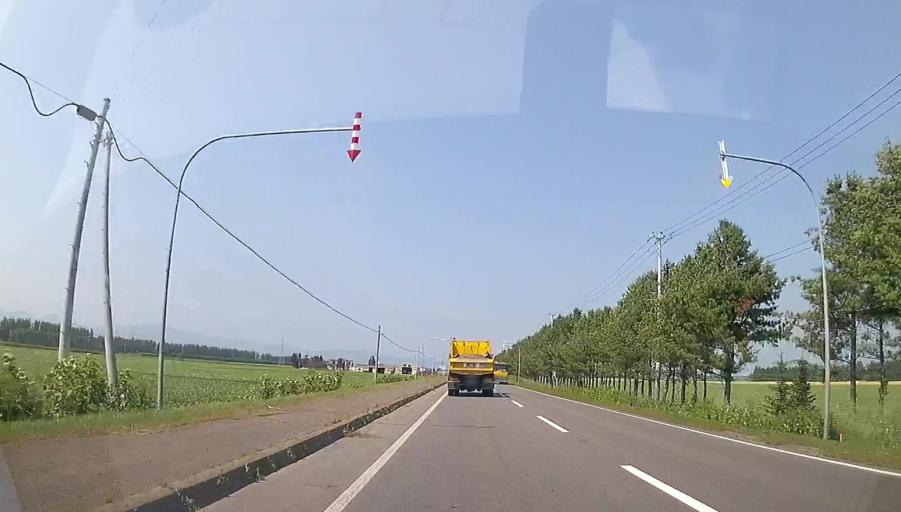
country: JP
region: Hokkaido
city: Otofuke
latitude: 43.1319
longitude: 143.2376
